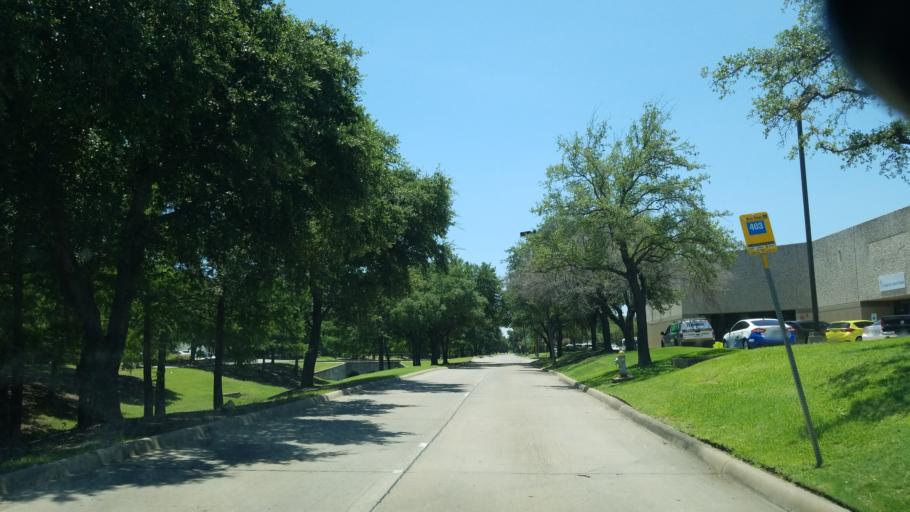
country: US
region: Texas
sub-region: Dallas County
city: Farmers Branch
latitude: 32.9317
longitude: -96.9153
